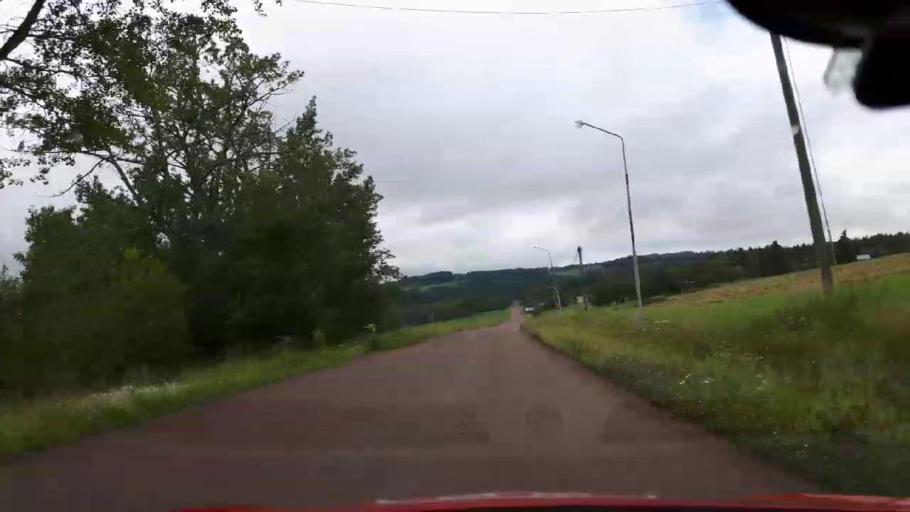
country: SE
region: Jaemtland
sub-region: Krokoms Kommun
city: Valla
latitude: 63.3879
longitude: 13.9080
